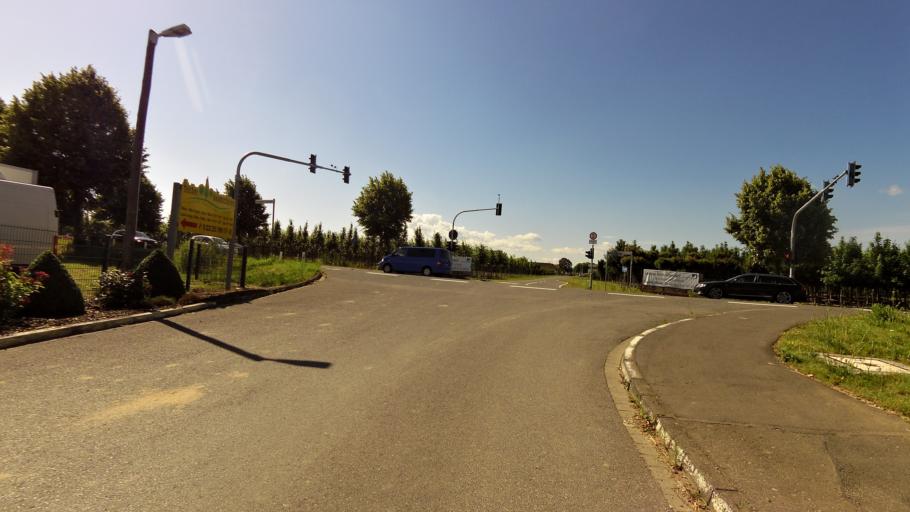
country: DE
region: North Rhine-Westphalia
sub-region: Regierungsbezirk Koln
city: Rheinbach
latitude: 50.6282
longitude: 6.9877
